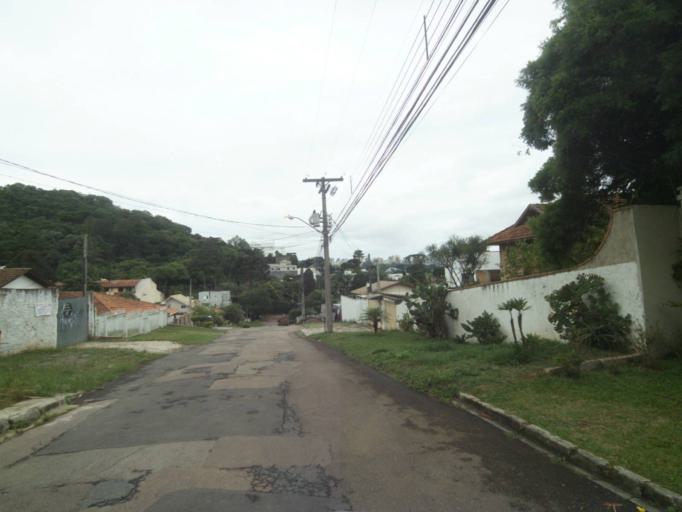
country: BR
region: Parana
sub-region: Curitiba
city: Curitiba
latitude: -25.4273
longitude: -49.3190
